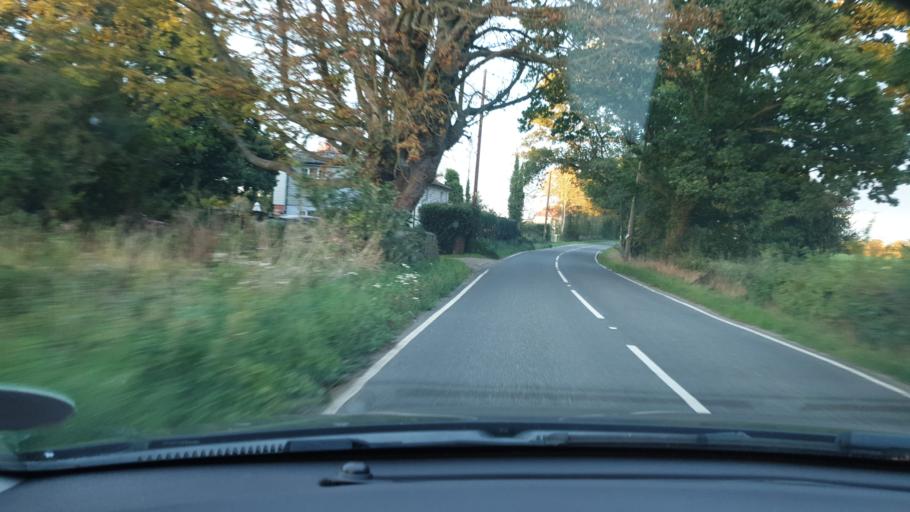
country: GB
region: England
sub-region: Essex
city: Alresford
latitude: 51.9055
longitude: 0.9939
